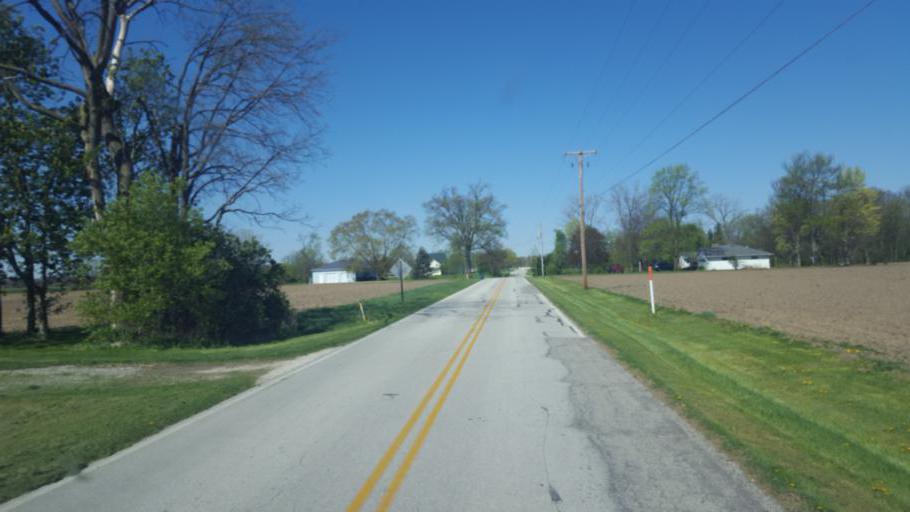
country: US
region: Ohio
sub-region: Seneca County
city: Tiffin
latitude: 41.2112
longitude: -83.1698
